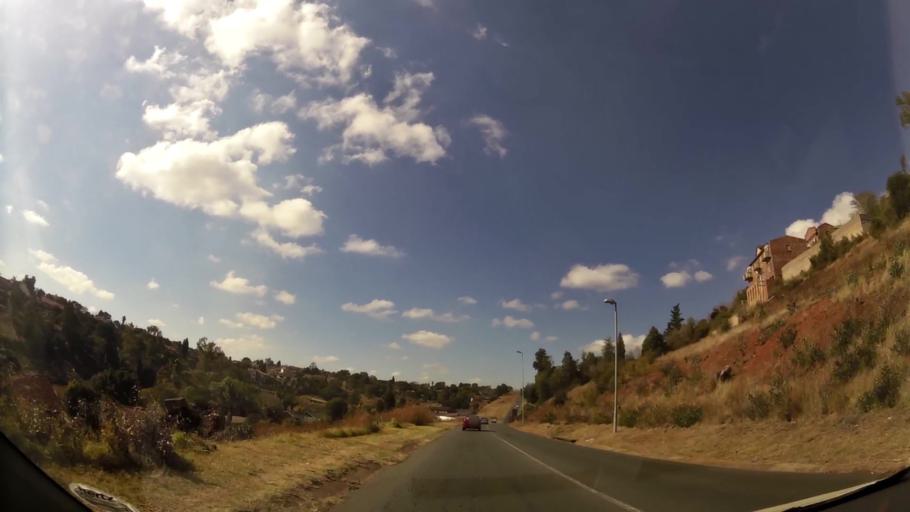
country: ZA
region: Gauteng
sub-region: City of Johannesburg Metropolitan Municipality
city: Roodepoort
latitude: -26.1136
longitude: 27.8446
